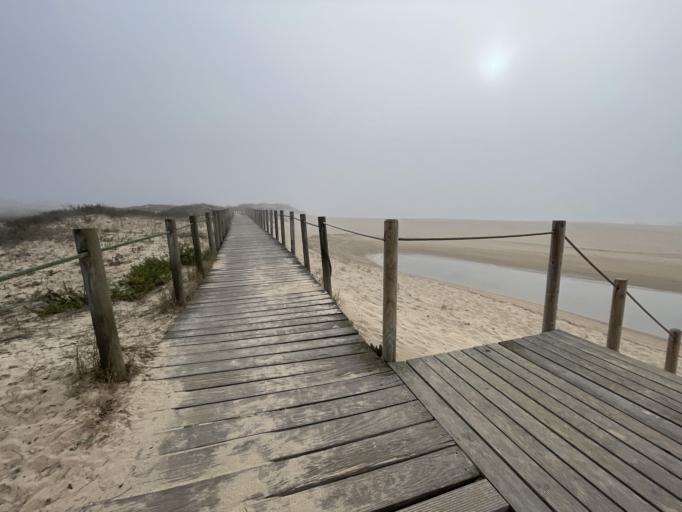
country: PT
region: Porto
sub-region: Vila Nova de Gaia
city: Vila Nova da Telha
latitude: 41.0779
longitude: -8.6566
